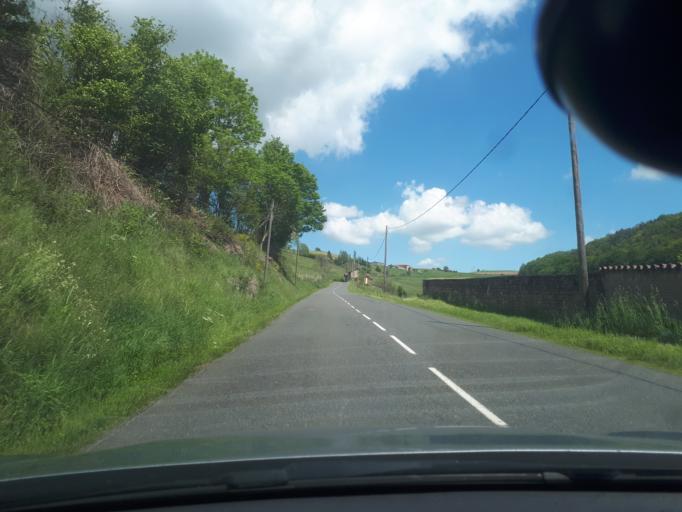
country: FR
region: Rhone-Alpes
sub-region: Departement du Rhone
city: Aveize
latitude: 45.6899
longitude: 4.5107
